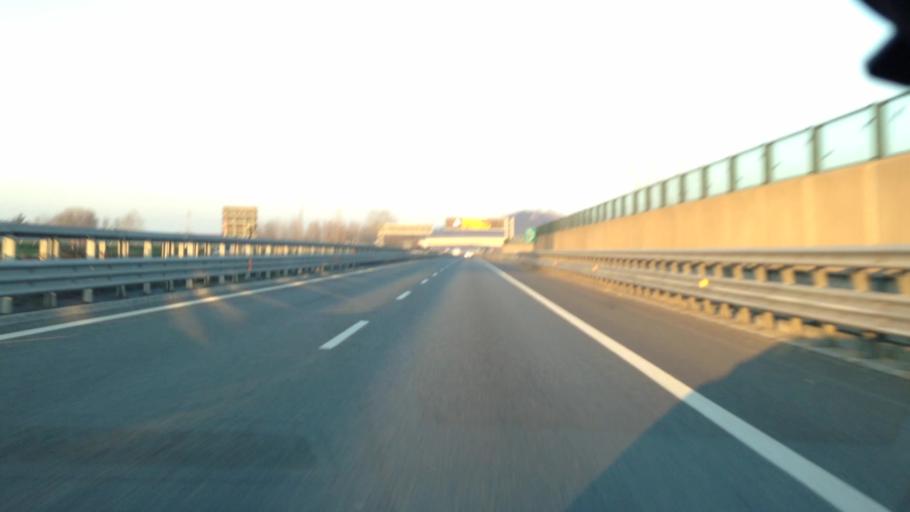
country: IT
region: Piedmont
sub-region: Provincia di Asti
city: Isola d'Asti
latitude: 44.8506
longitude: 8.1948
